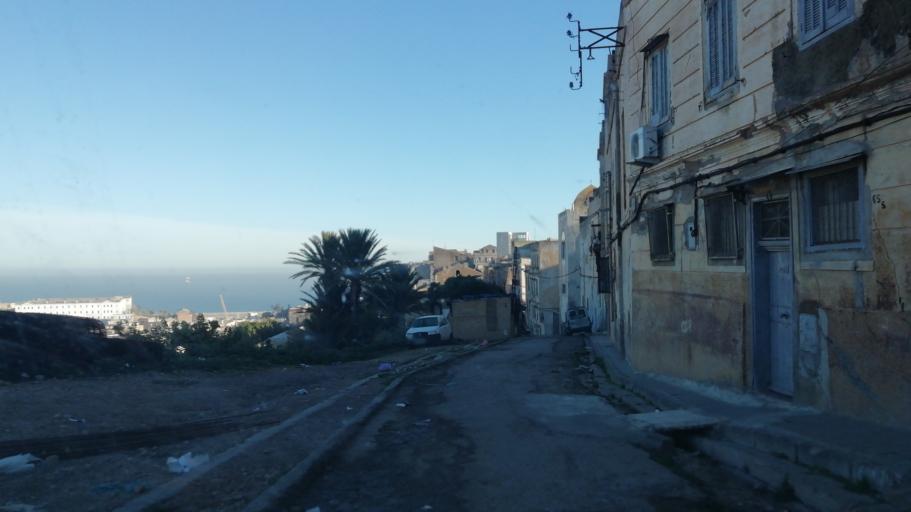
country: DZ
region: Oran
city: Oran
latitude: 35.6998
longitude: -0.6529
